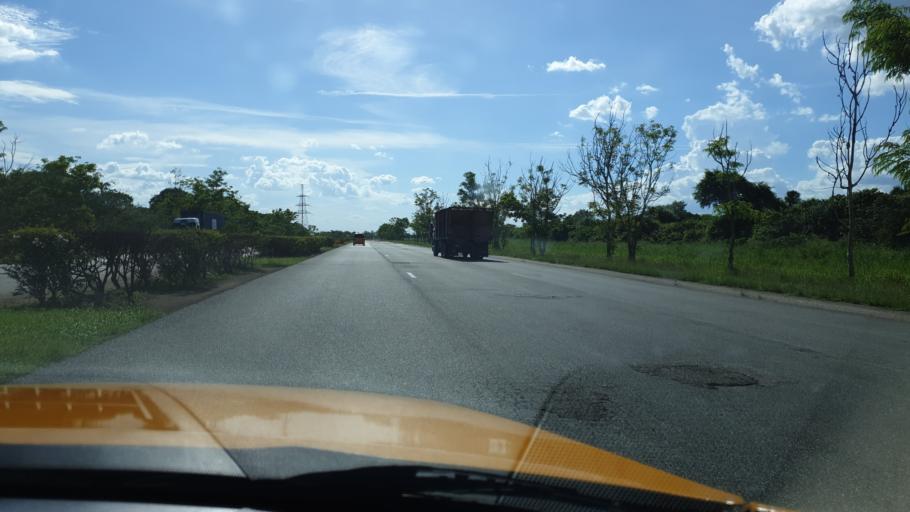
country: CU
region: Cienfuegos
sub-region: Municipio de Aguada de Pasajeros
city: Aguada de Pasajeros
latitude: 22.4079
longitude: -80.8819
